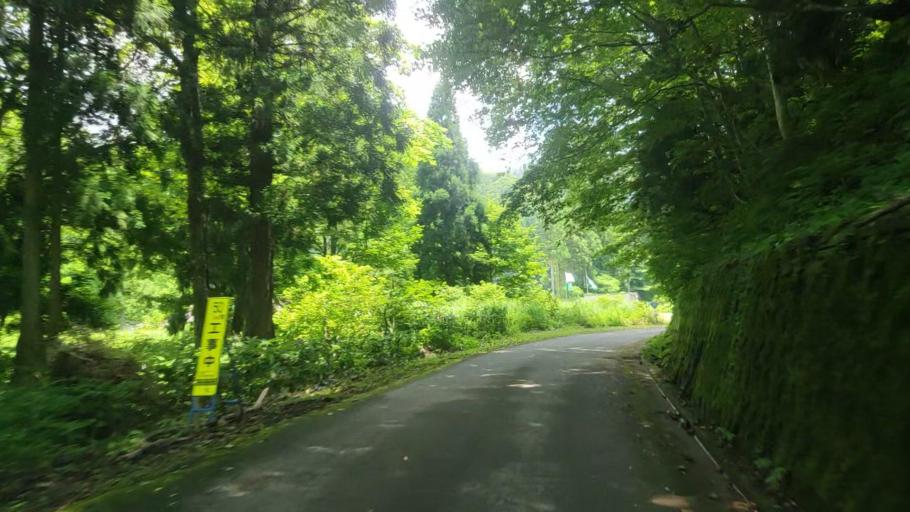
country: JP
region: Fukui
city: Ono
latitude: 35.8208
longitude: 136.4511
